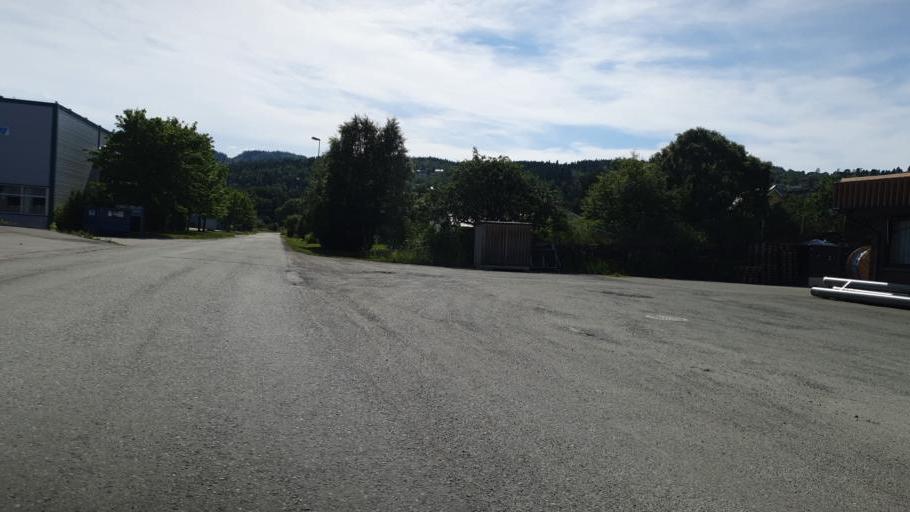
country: NO
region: Nord-Trondelag
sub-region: Leksvik
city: Leksvik
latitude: 63.6686
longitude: 10.6166
